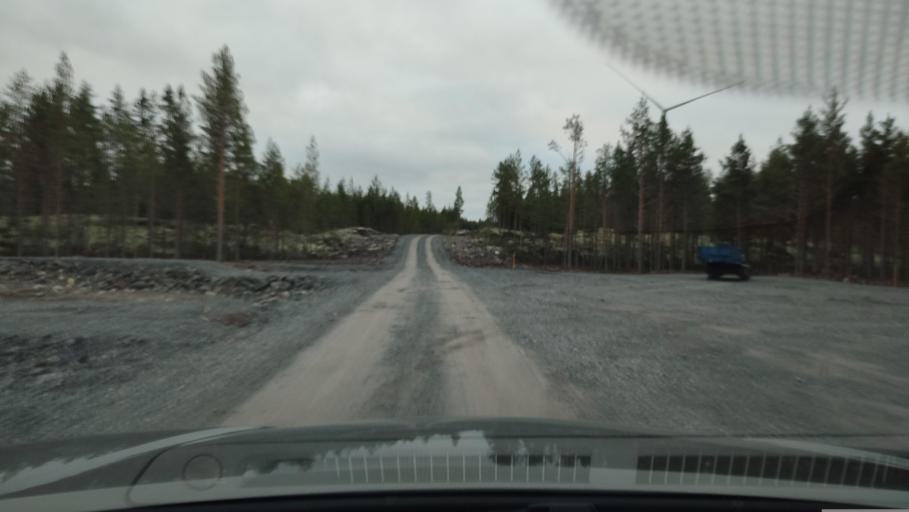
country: FI
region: Southern Ostrobothnia
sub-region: Suupohja
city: Karijoki
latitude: 62.1865
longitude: 21.5737
